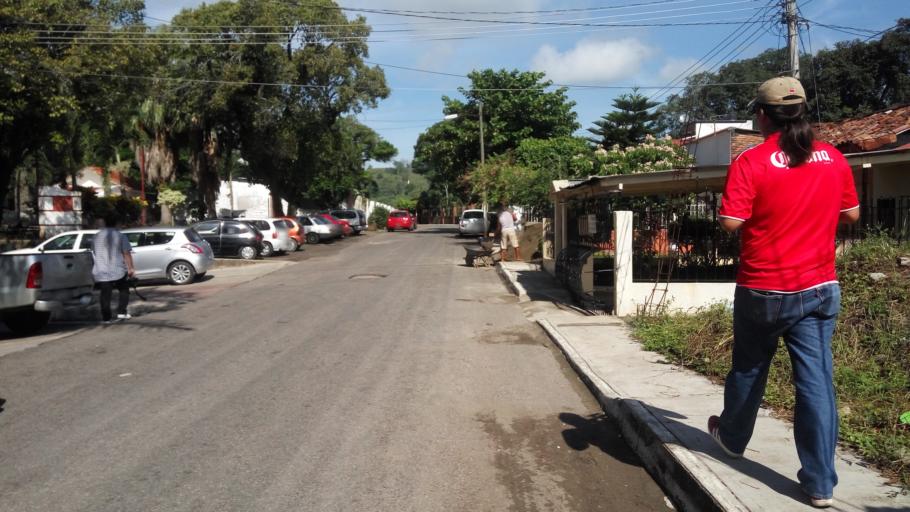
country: MX
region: Tabasco
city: Teapa
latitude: 17.5457
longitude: -92.9566
